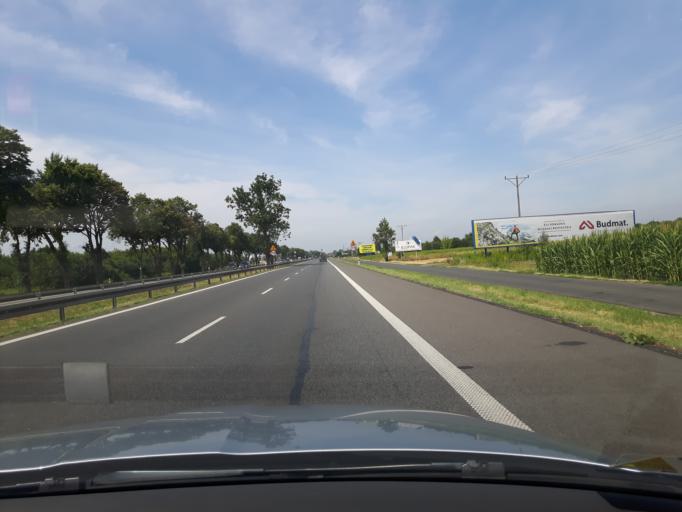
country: PL
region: Masovian Voivodeship
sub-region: Powiat nowodworski
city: Nowy Dwor Mazowiecki
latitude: 52.3823
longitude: 20.7588
